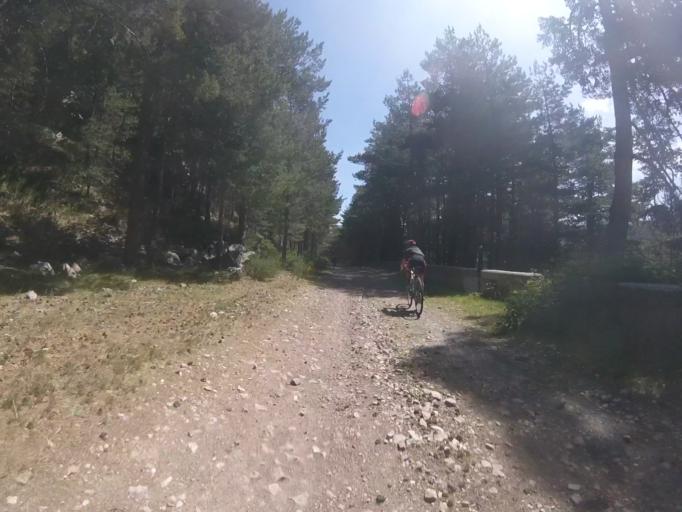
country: ES
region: Madrid
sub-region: Provincia de Madrid
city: Cercedilla
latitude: 40.7988
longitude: -4.0611
